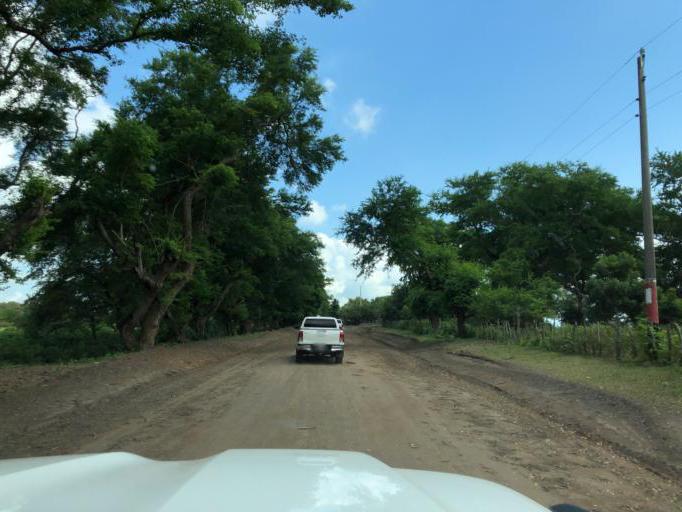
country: NI
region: Granada
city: Granada
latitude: 12.0042
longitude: -85.9342
